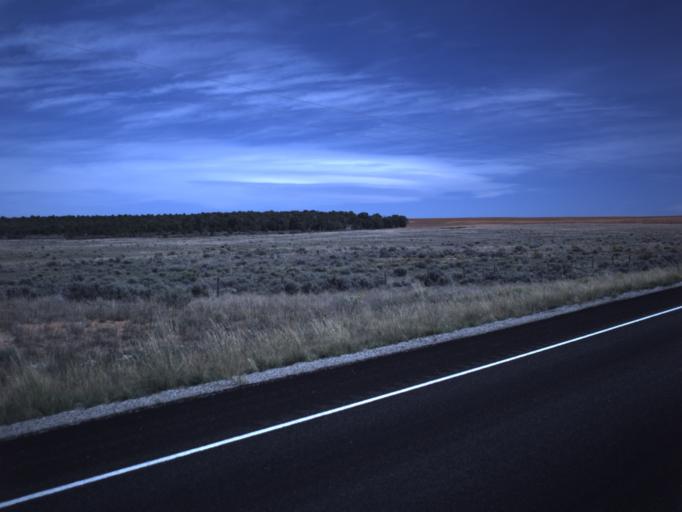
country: US
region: Utah
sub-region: San Juan County
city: Monticello
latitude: 37.8491
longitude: -109.1605
